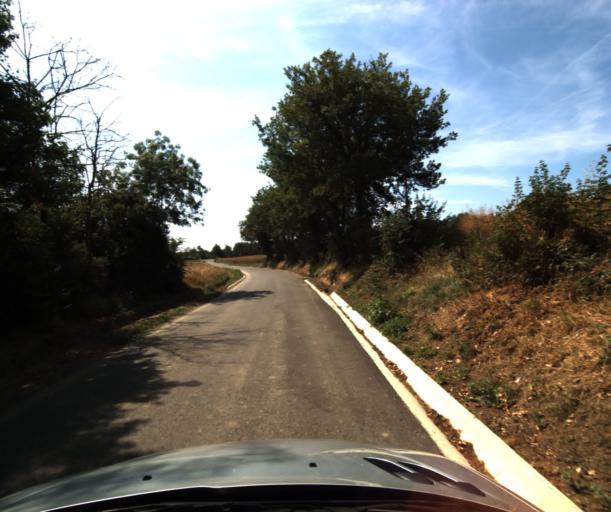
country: FR
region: Midi-Pyrenees
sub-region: Departement de la Haute-Garonne
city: Labastidette
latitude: 43.4709
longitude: 1.2190
